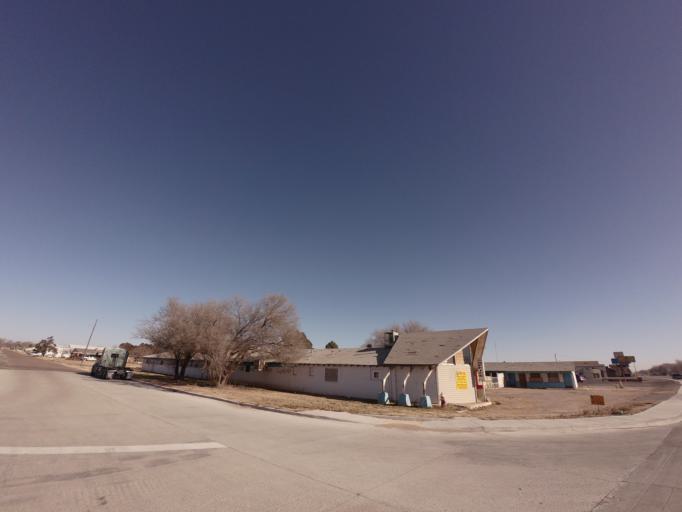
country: US
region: New Mexico
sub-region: Curry County
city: Clovis
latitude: 34.3969
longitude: -103.1851
